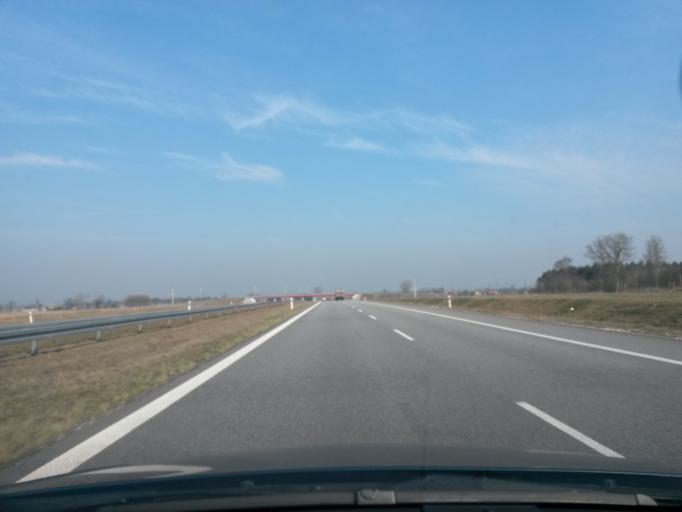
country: PL
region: Lodz Voivodeship
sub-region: Powiat kutnowski
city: Krzyzanow
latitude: 52.1952
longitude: 19.4872
